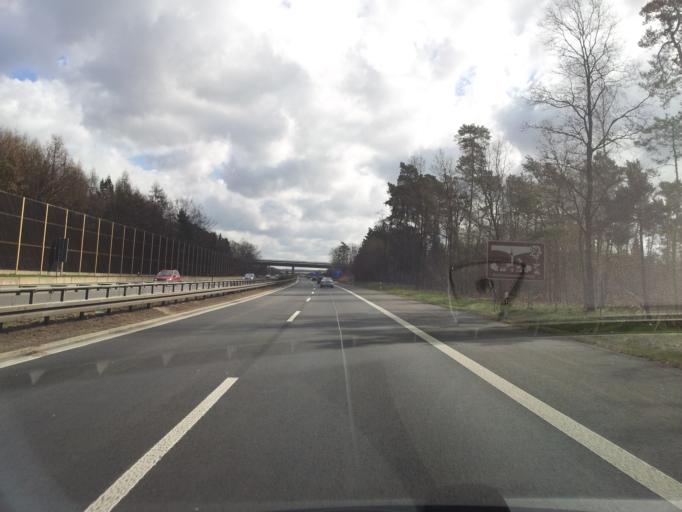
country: DE
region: Saxony
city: Ottendorf-Okrilla
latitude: 51.1710
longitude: 13.8324
